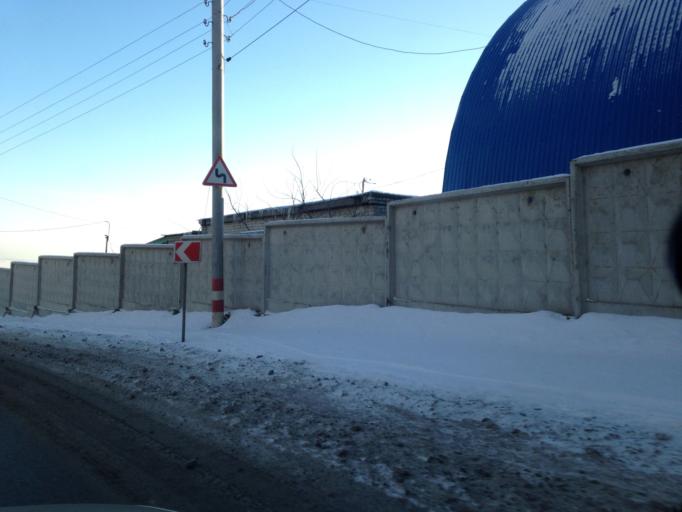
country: RU
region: Ulyanovsk
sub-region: Ulyanovskiy Rayon
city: Ulyanovsk
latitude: 54.3050
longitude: 48.3906
